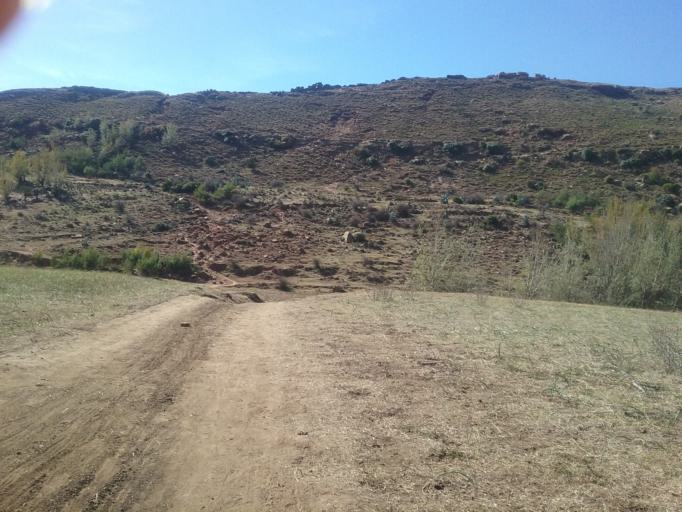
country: LS
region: Maseru
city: Nako
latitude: -29.4795
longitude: 27.6447
